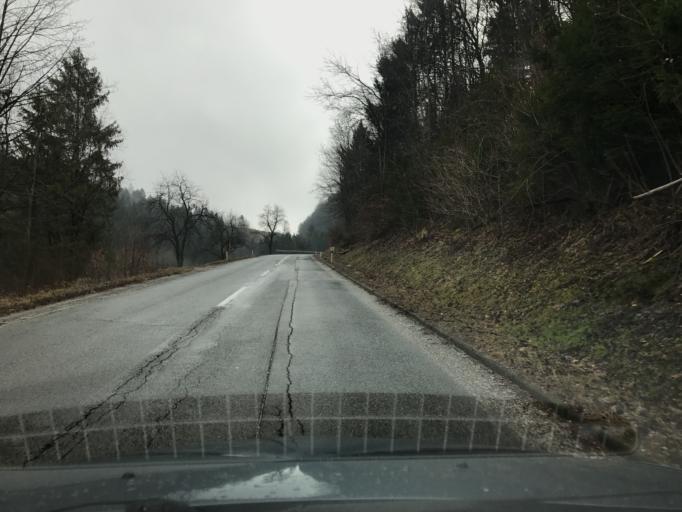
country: SI
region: Gornji Grad
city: Gornji Grad
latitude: 46.2158
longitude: 14.7976
